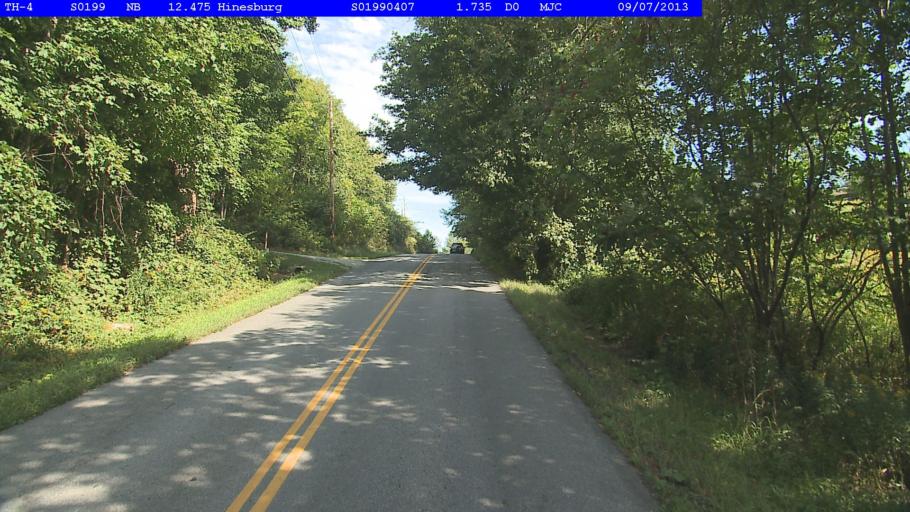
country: US
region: Vermont
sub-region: Chittenden County
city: Hinesburg
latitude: 44.3030
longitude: -73.1093
